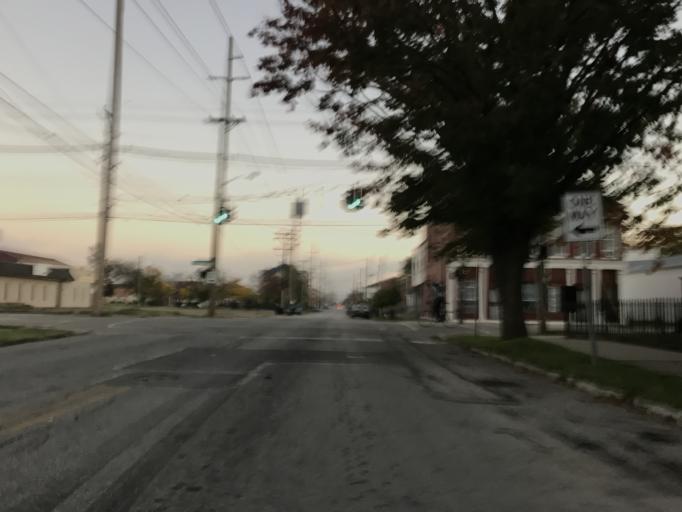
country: US
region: Kentucky
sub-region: Jefferson County
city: Louisville
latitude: 38.2399
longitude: -85.7424
